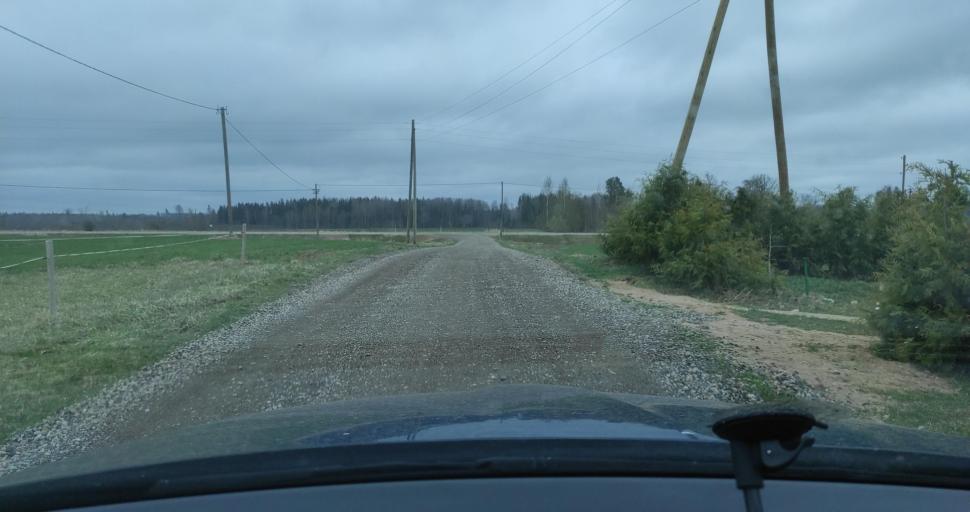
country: LV
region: Saldus Rajons
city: Saldus
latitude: 56.6297
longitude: 22.4279
